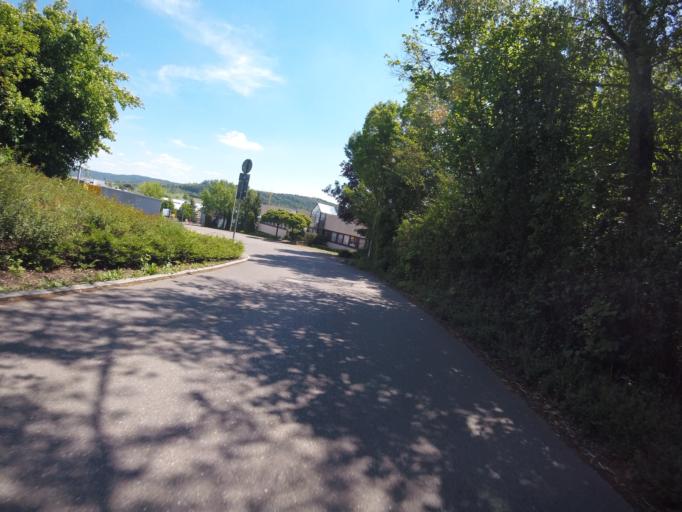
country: DE
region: Baden-Wuerttemberg
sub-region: Regierungsbezirk Stuttgart
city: Backnang
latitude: 48.9163
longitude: 9.4244
